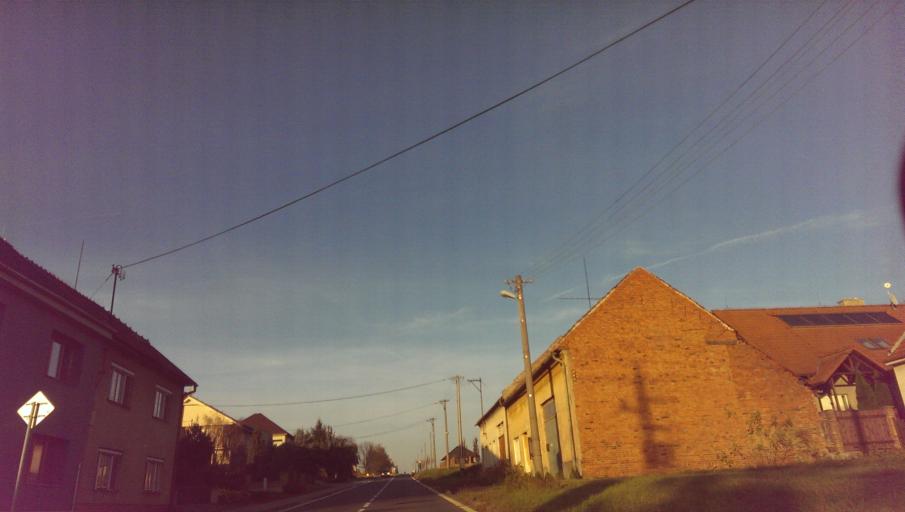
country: CZ
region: Zlin
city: Bilovice
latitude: 49.1028
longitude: 17.5558
